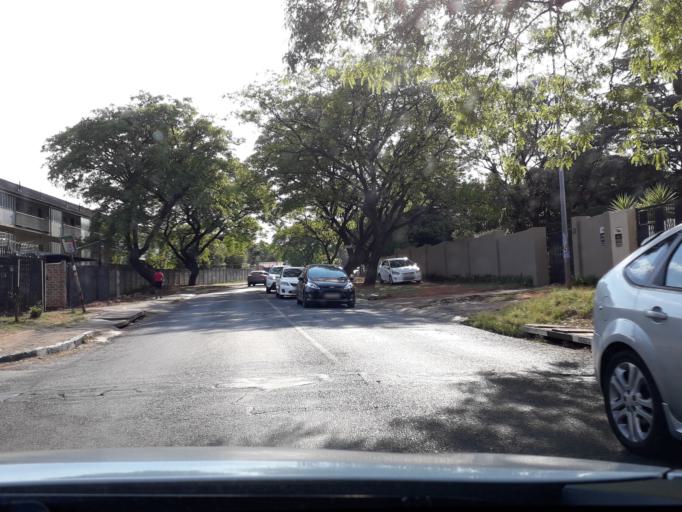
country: ZA
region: Gauteng
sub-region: City of Johannesburg Metropolitan Municipality
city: Johannesburg
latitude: -26.1253
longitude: 27.9769
